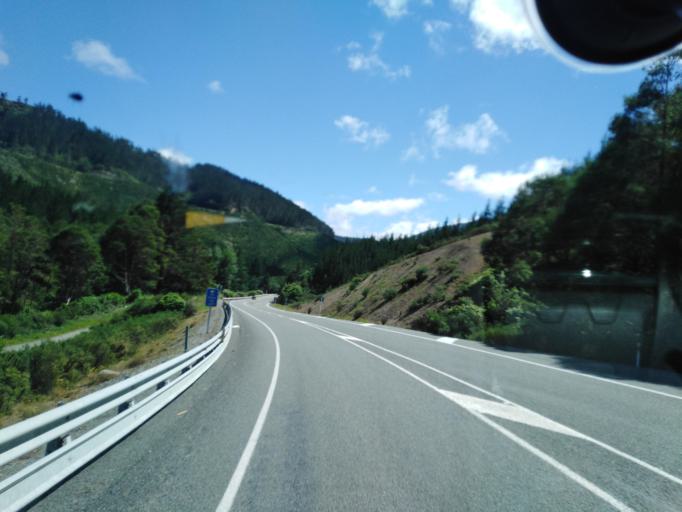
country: NZ
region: Nelson
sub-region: Nelson City
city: Nelson
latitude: -41.1841
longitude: 173.5600
